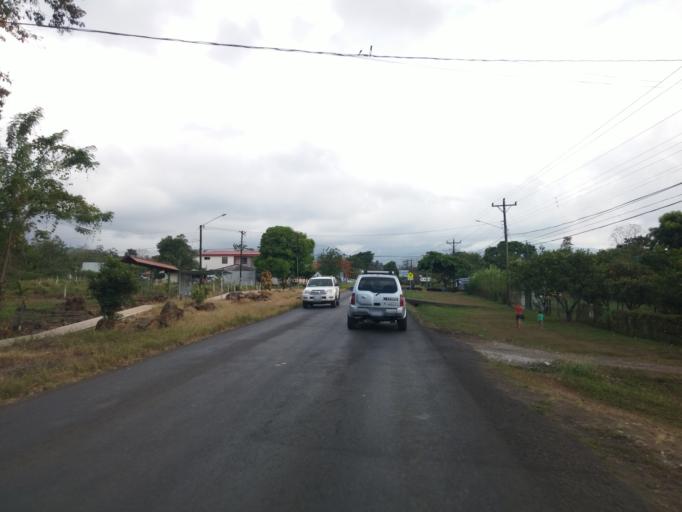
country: CR
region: Alajuela
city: Pital
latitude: 10.4049
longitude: -84.3369
